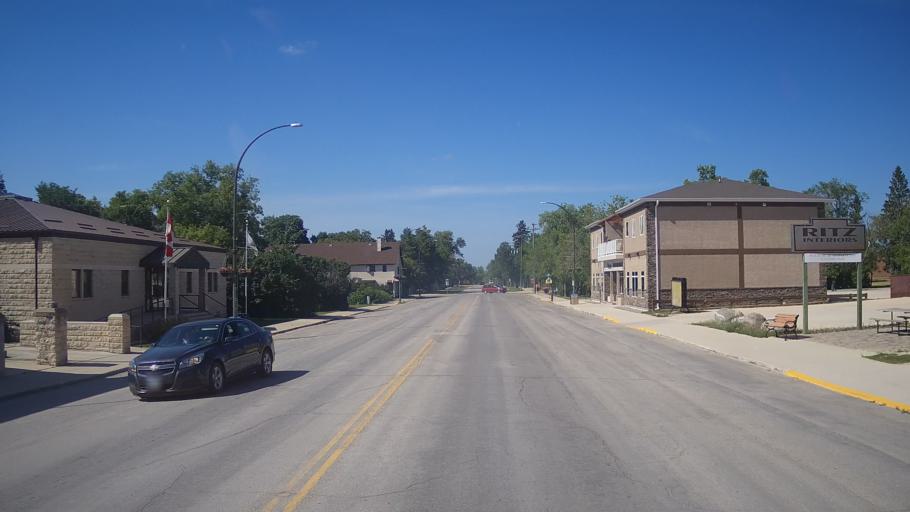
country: CA
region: Manitoba
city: Stonewall
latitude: 50.1363
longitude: -97.3266
